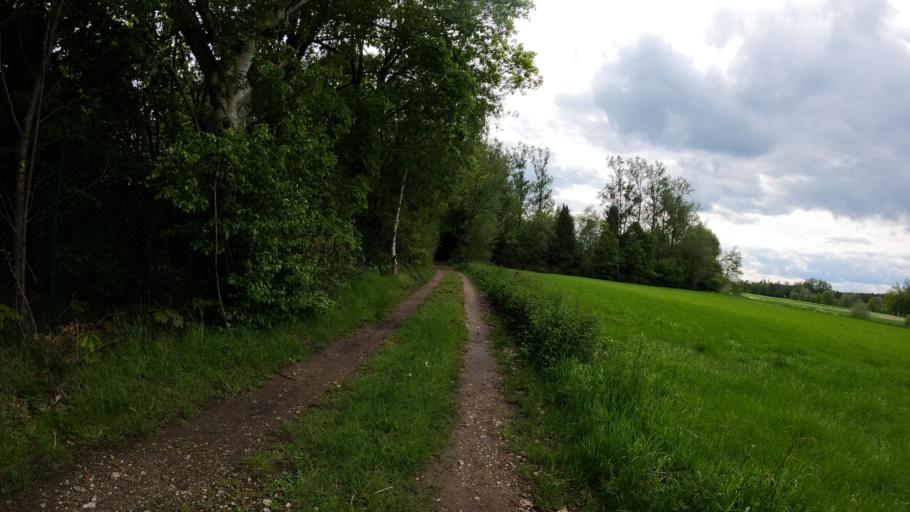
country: BE
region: Flanders
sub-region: Provincie Antwerpen
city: Vosselaar
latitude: 51.2860
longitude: 4.9109
